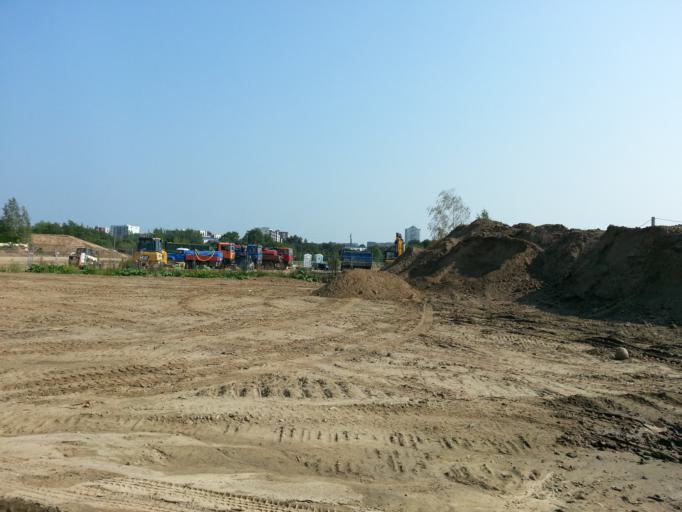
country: LT
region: Vilnius County
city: Pasilaiciai
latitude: 54.7290
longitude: 25.2060
